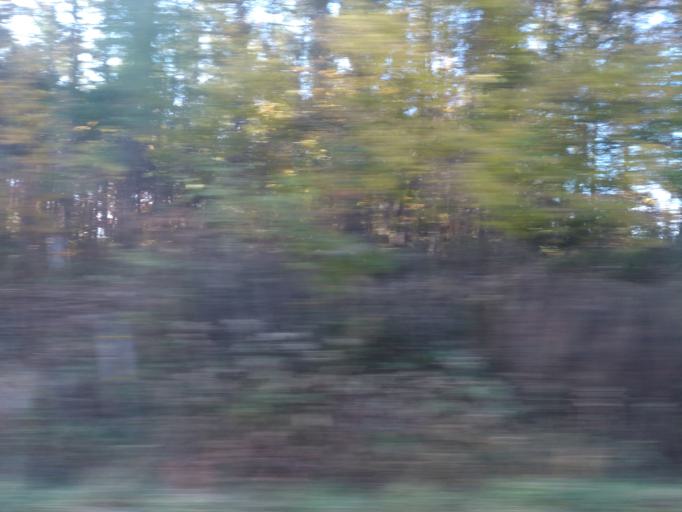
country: JP
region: Hokkaido
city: Kitahiroshima
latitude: 42.9503
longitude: 141.5710
